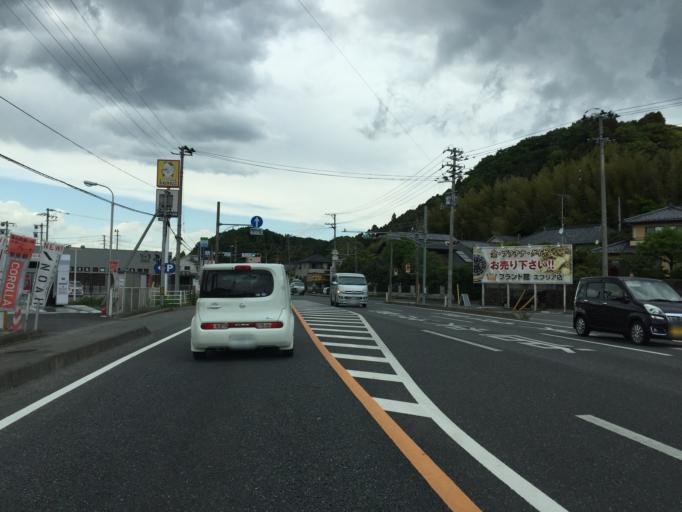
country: JP
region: Fukushima
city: Iwaki
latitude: 36.9877
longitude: 140.8685
